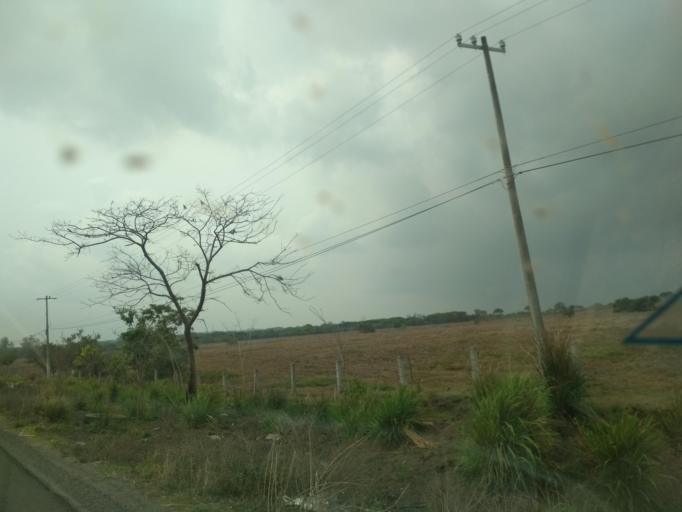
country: MX
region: Veracruz
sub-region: Medellin
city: La Laguna y Monte del Castillo
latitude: 19.0030
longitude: -96.1089
